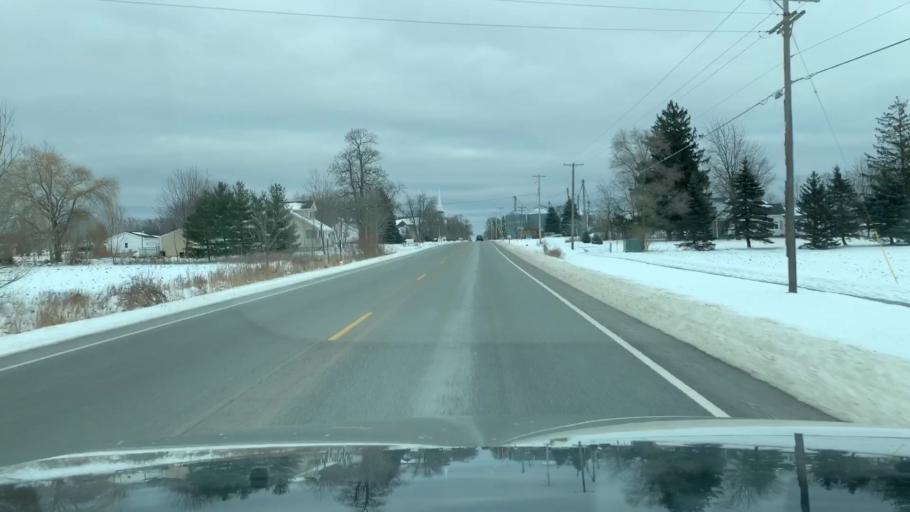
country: US
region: Michigan
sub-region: Ottawa County
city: Zeeland
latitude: 42.8120
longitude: -85.9466
